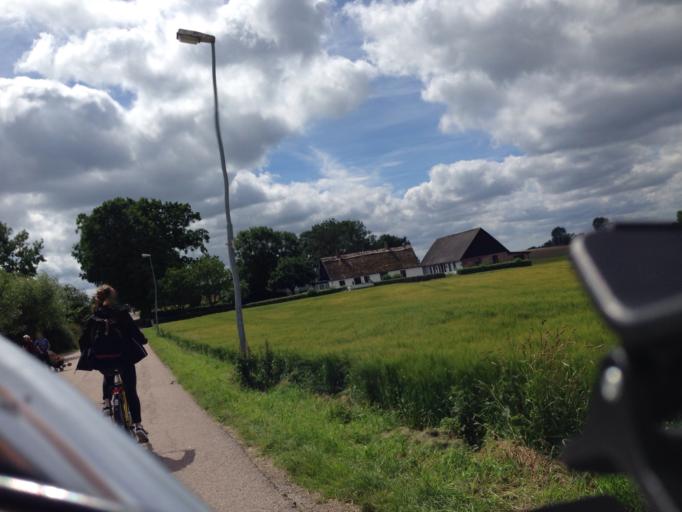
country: SE
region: Skane
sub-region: Helsingborg
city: Rydeback
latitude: 55.9149
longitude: 12.6871
